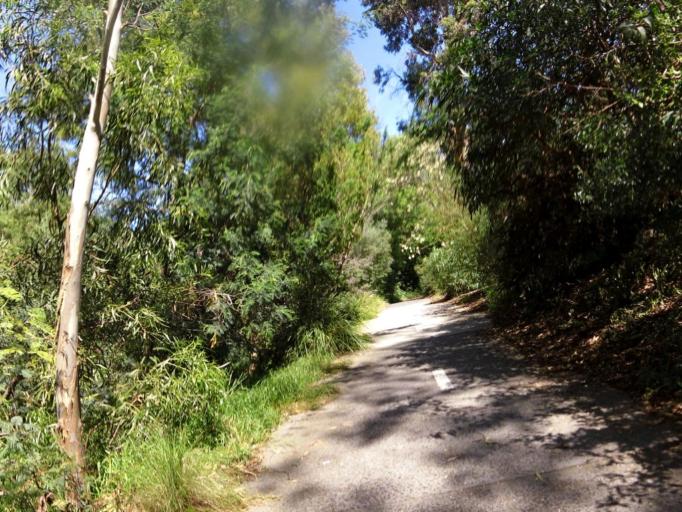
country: AU
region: Victoria
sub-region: Yarra
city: Clifton Hill
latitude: -37.7848
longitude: 144.9995
